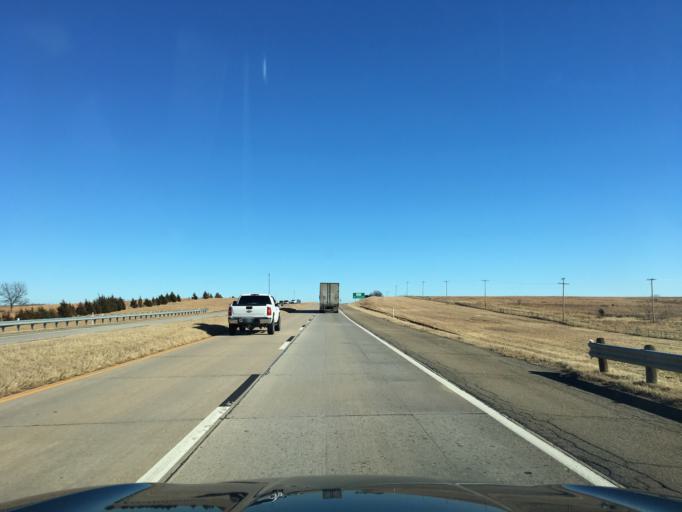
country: US
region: Oklahoma
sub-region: Pawnee County
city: Pawnee
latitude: 36.2248
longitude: -96.7661
